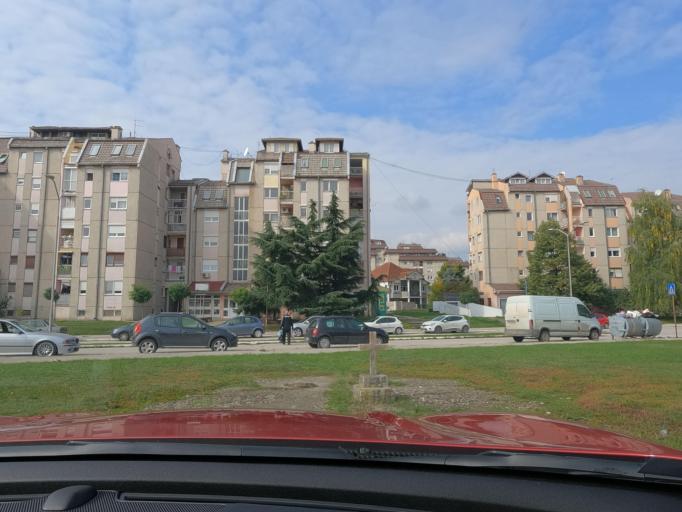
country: RS
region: Central Serbia
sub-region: Moravicki Okrug
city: Cacak
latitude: 43.8852
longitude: 20.3428
